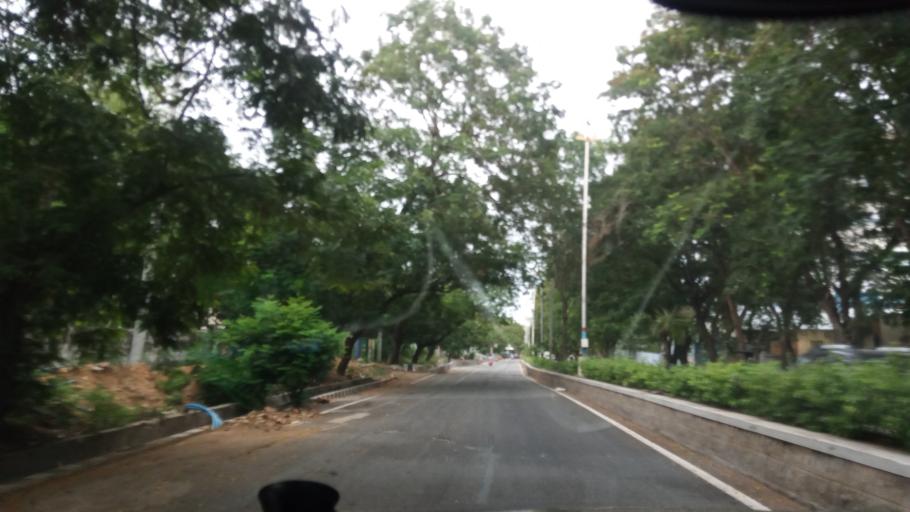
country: IN
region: Andhra Pradesh
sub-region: Chittoor
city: Akkarampalle
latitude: 13.6469
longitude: 79.4126
